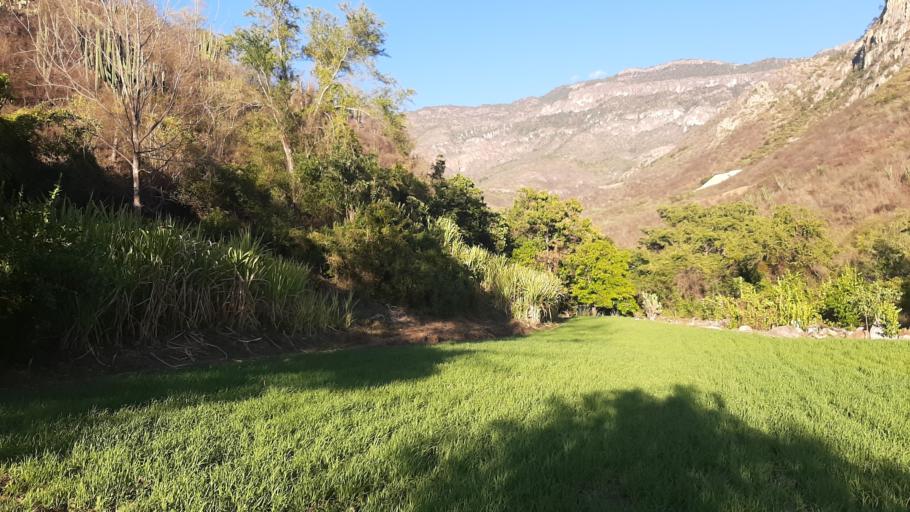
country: MX
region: Chihuahua
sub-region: Guadalupe y Calvo
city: Las Yerbitas [Aserradero]
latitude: 25.4306
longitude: -106.4719
